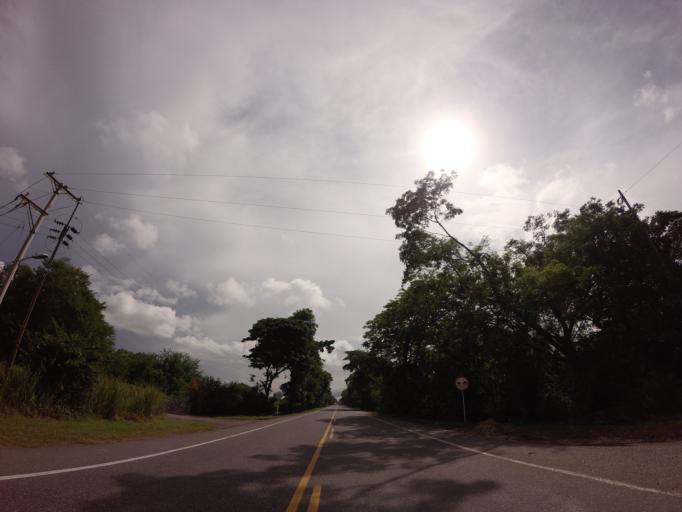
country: CO
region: Caldas
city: La Dorada
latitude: 5.3455
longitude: -74.7343
